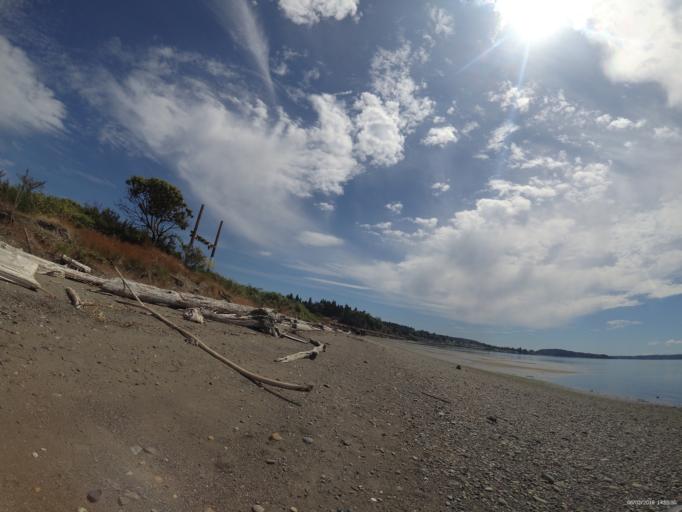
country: US
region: Washington
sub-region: Pierce County
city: Steilacoom
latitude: 47.1913
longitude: -122.5835
